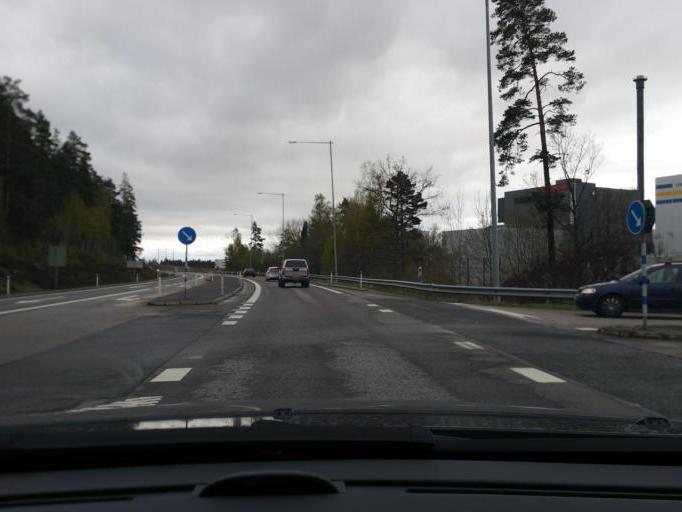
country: SE
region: Kronoberg
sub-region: Vaxjo Kommun
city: Vaexjoe
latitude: 56.8694
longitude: 14.8388
